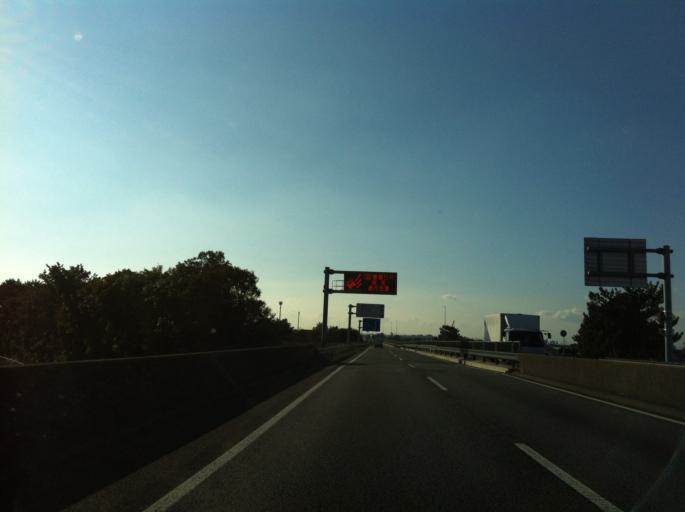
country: JP
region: Aichi
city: Kozakai-cho
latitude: 34.7686
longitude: 137.3323
